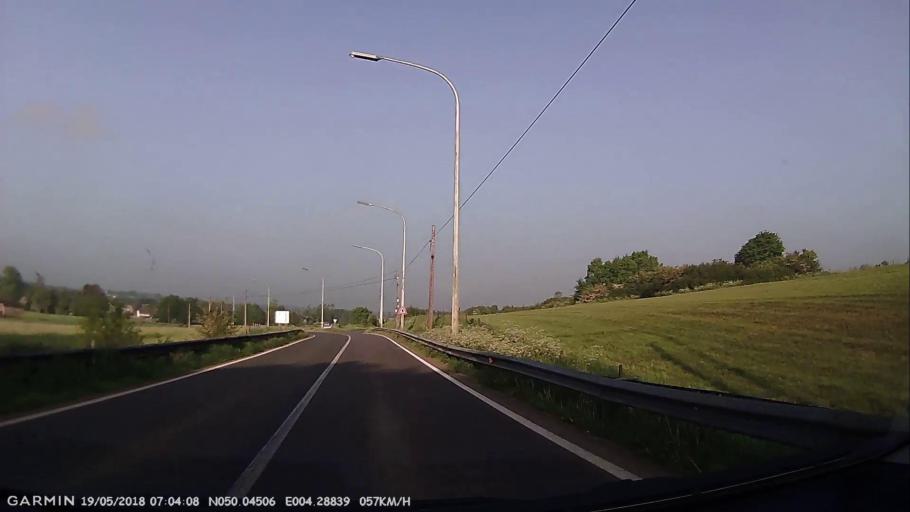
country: BE
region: Wallonia
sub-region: Province du Hainaut
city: Chimay
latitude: 50.0449
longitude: 4.2882
